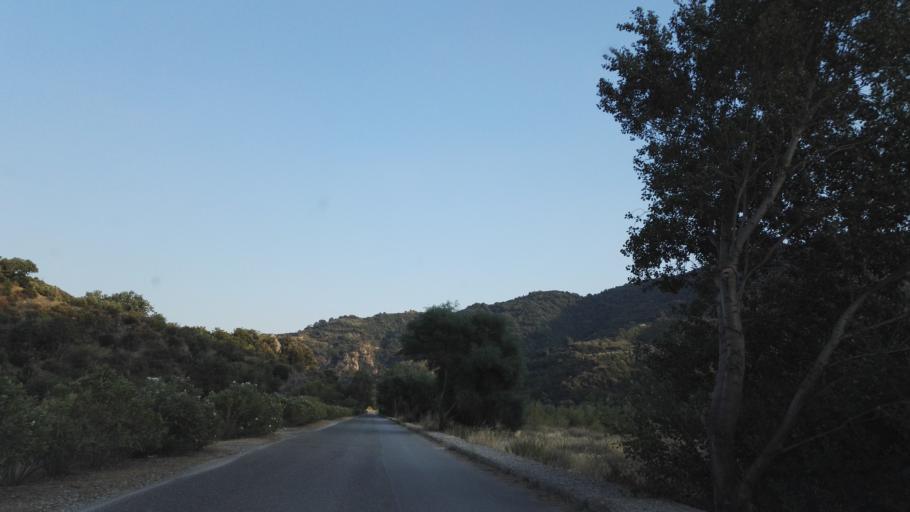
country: IT
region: Calabria
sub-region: Provincia di Reggio Calabria
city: Caulonia
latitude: 38.4117
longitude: 16.3834
